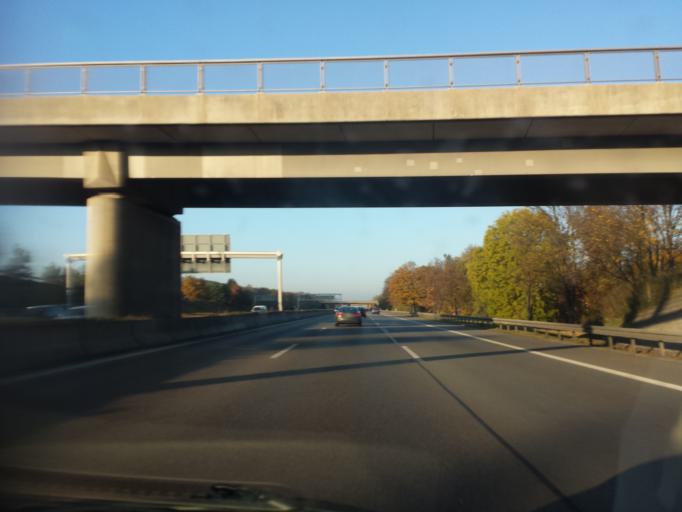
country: DE
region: Bavaria
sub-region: Upper Bavaria
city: Unterfoehring
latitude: 48.2167
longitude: 11.6272
